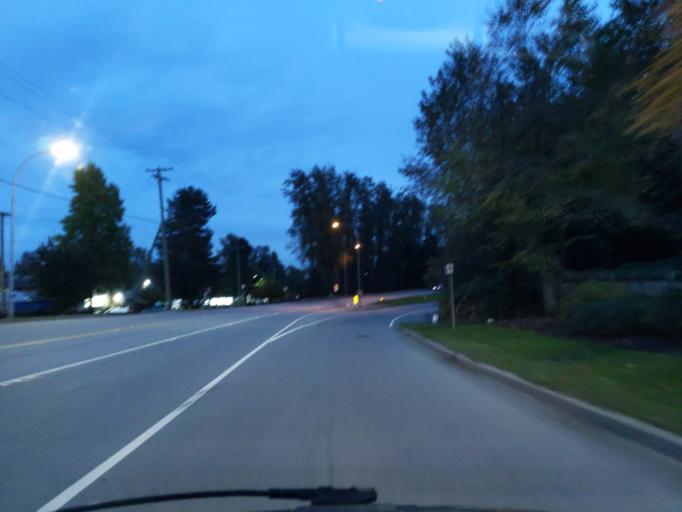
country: CA
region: British Columbia
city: Pitt Meadows
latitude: 49.1725
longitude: -122.6907
